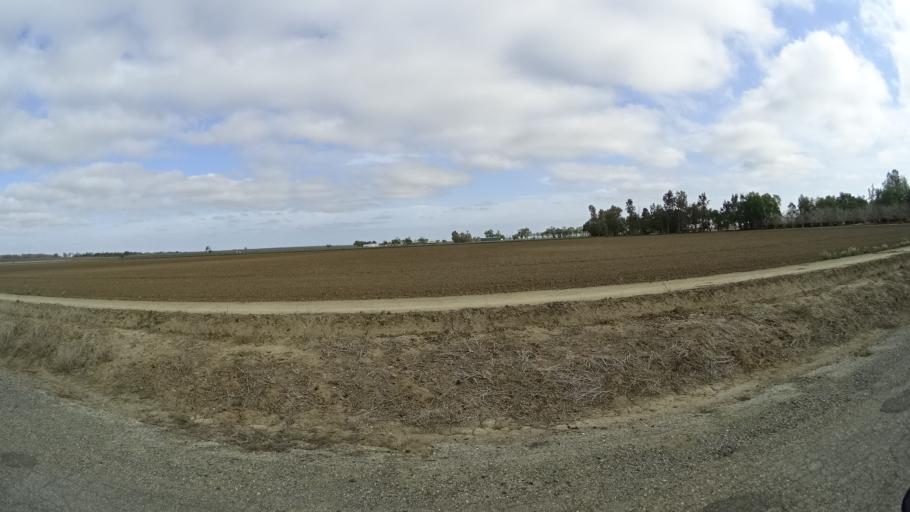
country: US
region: California
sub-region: Colusa County
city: Colusa
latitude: 39.4182
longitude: -121.9725
